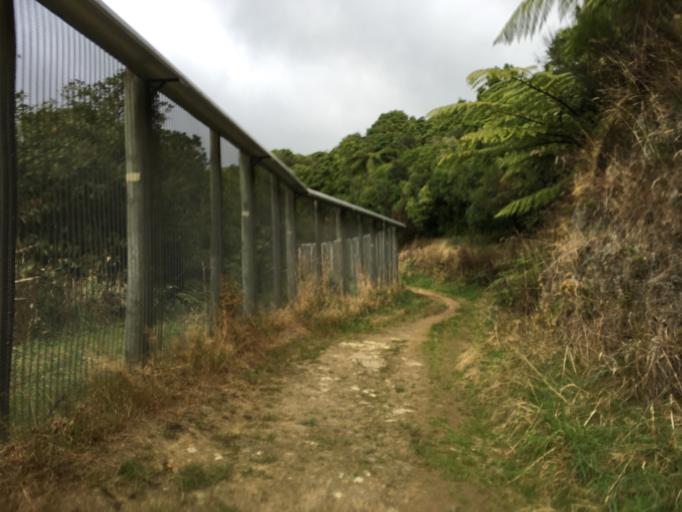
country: NZ
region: Wellington
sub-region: Wellington City
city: Brooklyn
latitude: -41.2968
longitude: 174.7394
